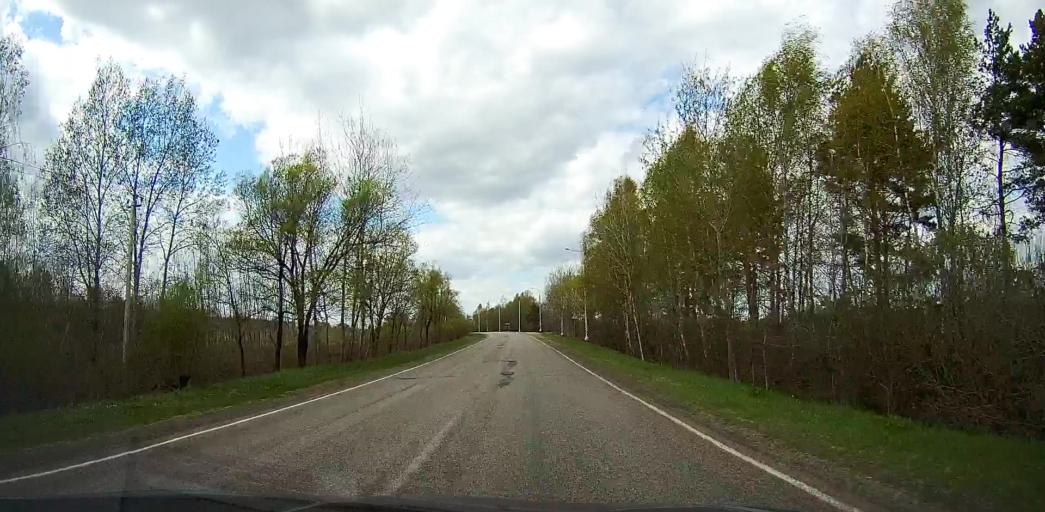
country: RU
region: Moskovskaya
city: Davydovo
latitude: 55.6628
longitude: 38.8062
